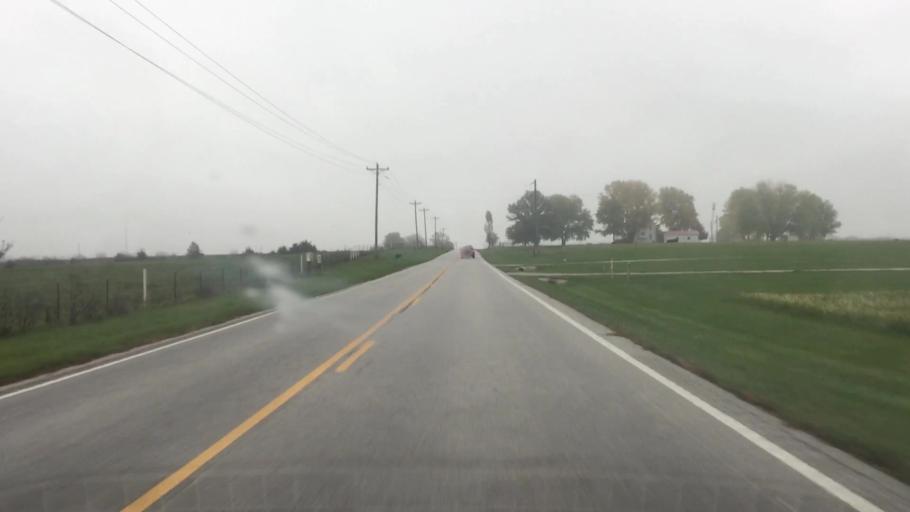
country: US
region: Missouri
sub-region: Callaway County
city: Fulton
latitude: 38.8739
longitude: -92.0637
